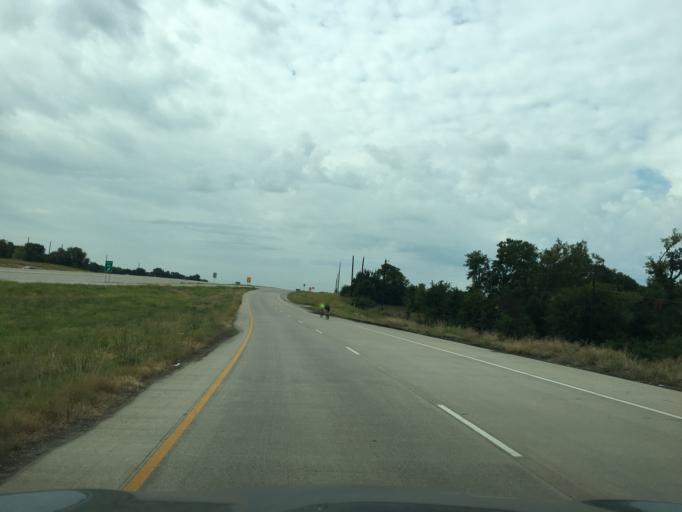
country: US
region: Texas
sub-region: Collin County
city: Melissa
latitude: 33.2840
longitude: -96.5932
